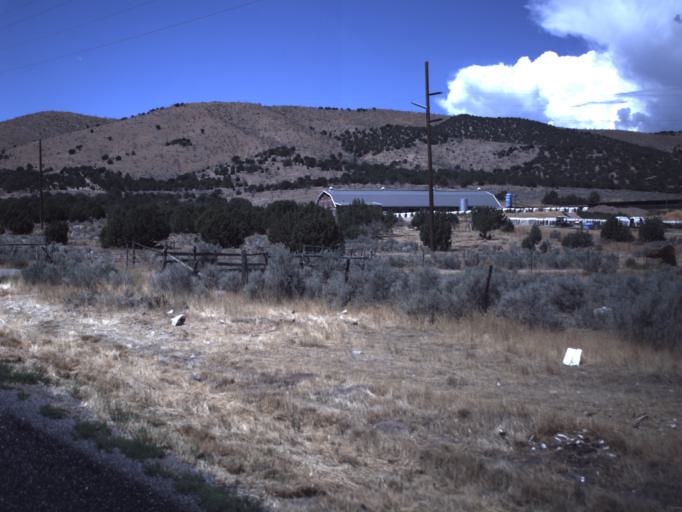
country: US
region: Utah
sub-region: Juab County
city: Nephi
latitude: 39.7029
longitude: -111.9215
